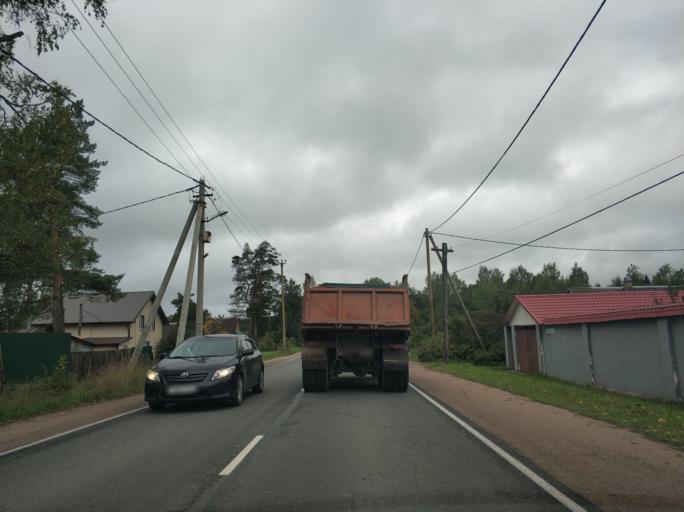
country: RU
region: Leningrad
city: Borisova Griva
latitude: 60.0846
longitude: 30.8907
